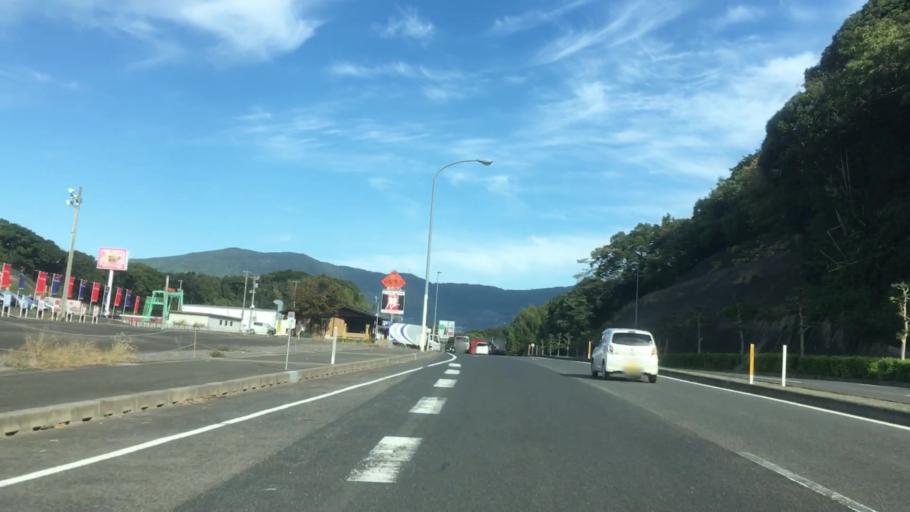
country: JP
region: Nagasaki
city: Sasebo
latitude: 33.1360
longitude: 129.7863
